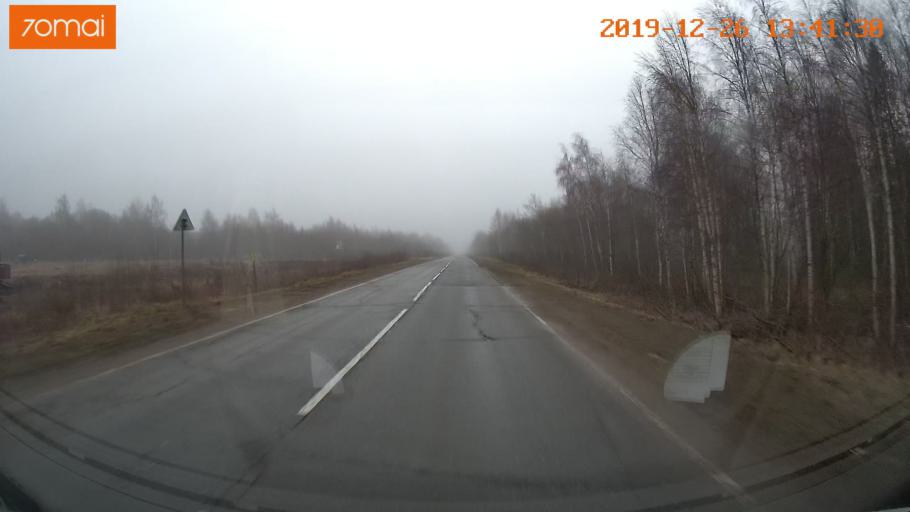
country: RU
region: Vologda
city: Sheksna
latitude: 58.7309
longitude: 38.4502
